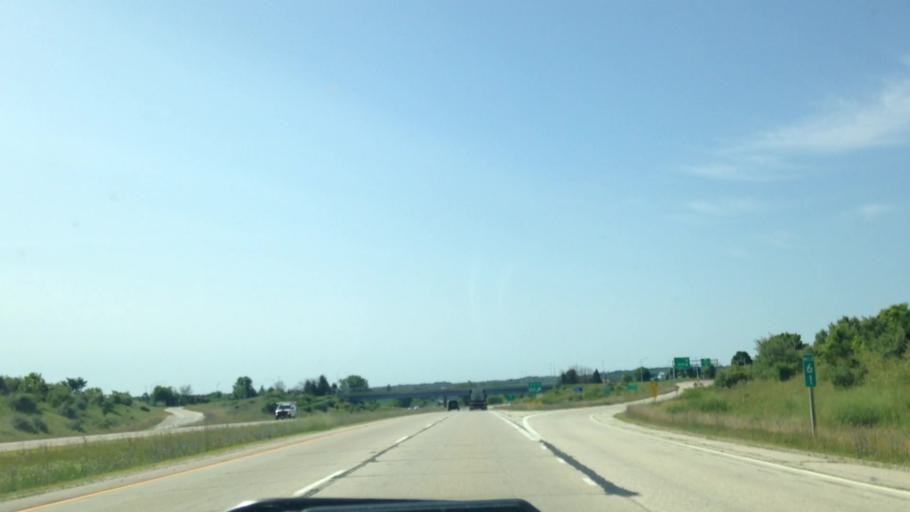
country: US
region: Wisconsin
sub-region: Washington County
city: Richfield
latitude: 43.2874
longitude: -88.1866
